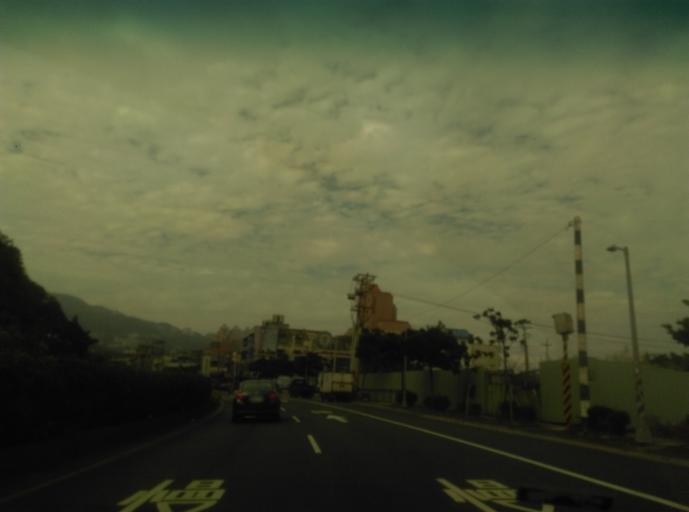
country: TW
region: Taiwan
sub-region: Keelung
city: Keelung
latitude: 25.1835
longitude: 121.6875
